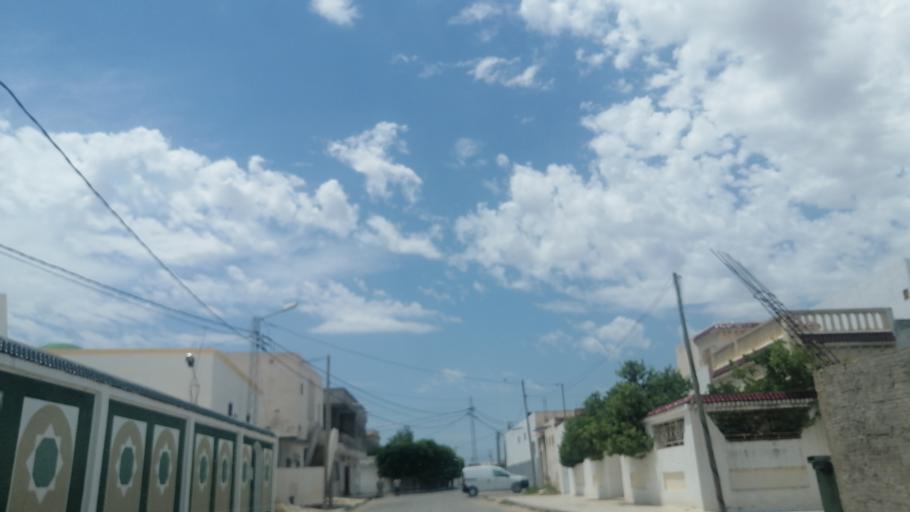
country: TN
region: Al Qayrawan
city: Sbikha
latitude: 36.1261
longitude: 10.0937
